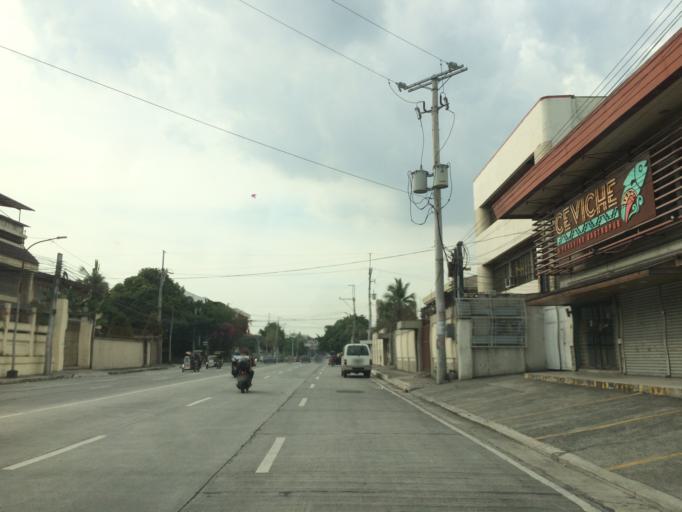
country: PH
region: Calabarzon
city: Del Monte
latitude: 14.6301
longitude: 121.0083
